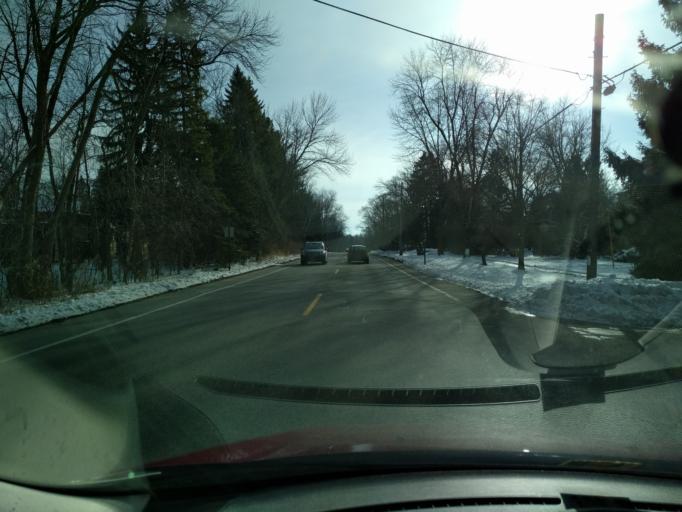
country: US
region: Wisconsin
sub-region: Milwaukee County
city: Fox Point
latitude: 43.1661
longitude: -87.8956
